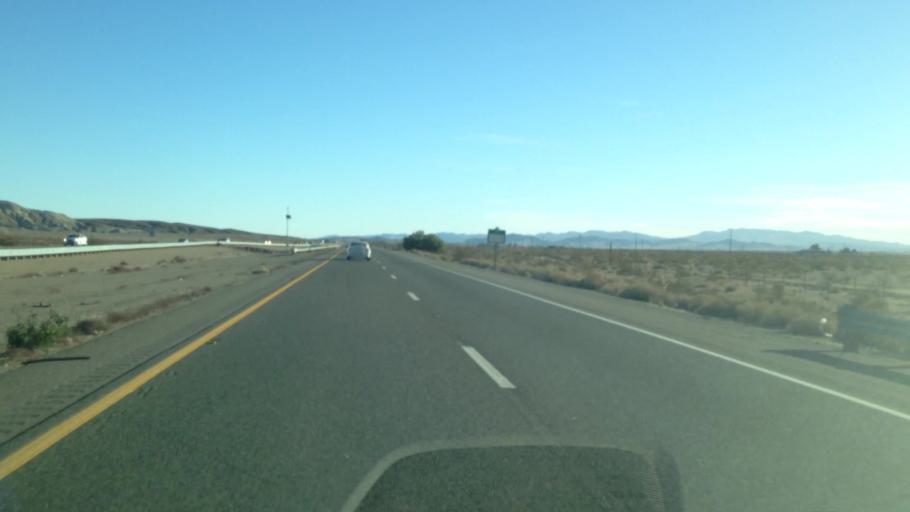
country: US
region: California
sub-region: San Bernardino County
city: Barstow
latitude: 34.9229
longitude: -116.7477
